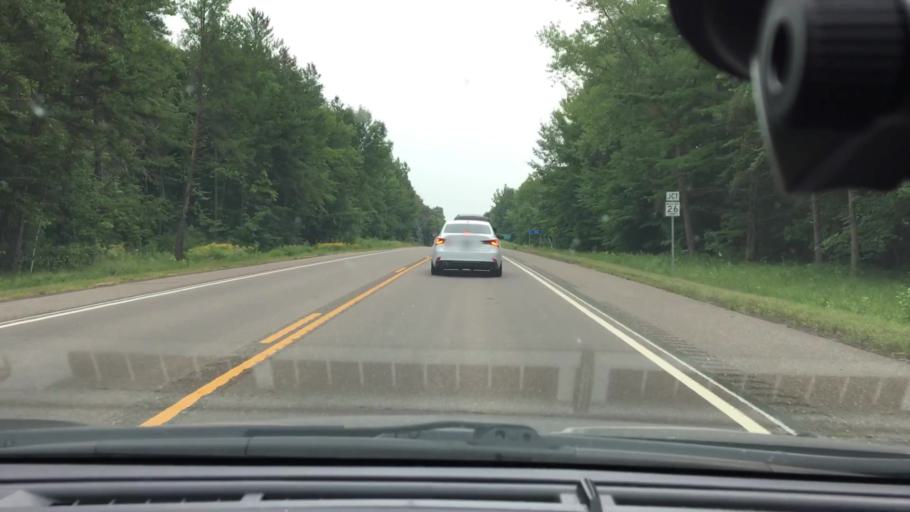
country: US
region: Minnesota
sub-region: Mille Lacs County
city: Vineland
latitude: 46.1473
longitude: -93.7310
